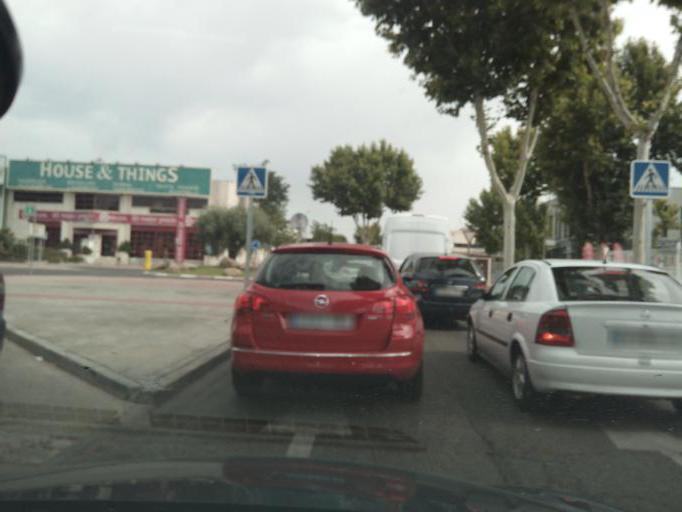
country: ES
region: Madrid
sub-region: Provincia de Madrid
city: Las Rozas de Madrid
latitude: 40.5017
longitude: -3.8891
